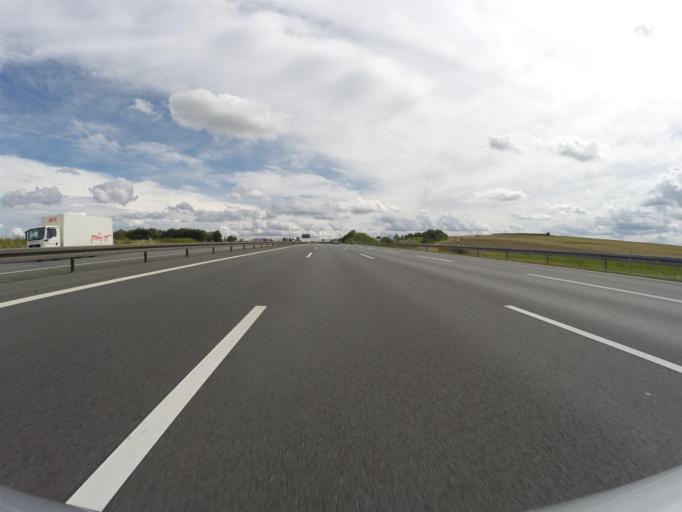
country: DE
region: Bavaria
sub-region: Upper Franconia
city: Leupoldsgrun
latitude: 50.3065
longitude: 11.8037
